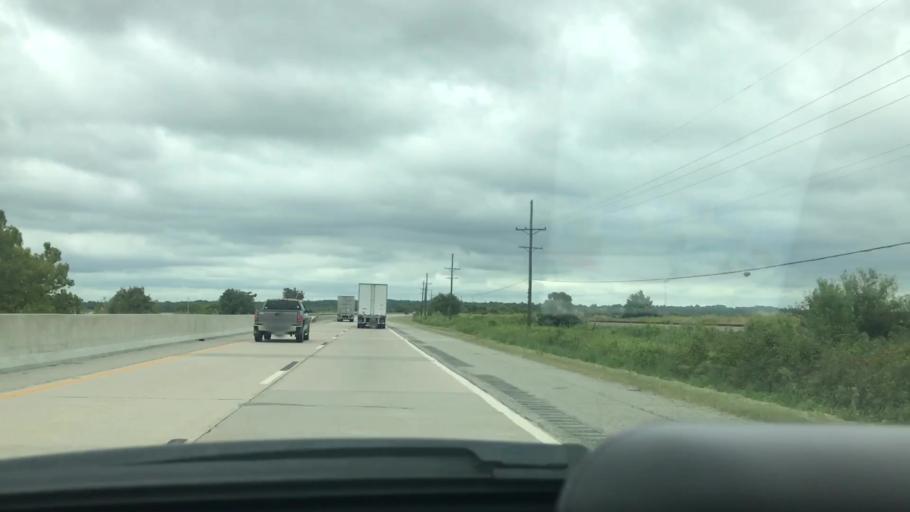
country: US
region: Oklahoma
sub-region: McIntosh County
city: Eufaula
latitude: 35.3351
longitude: -95.5867
